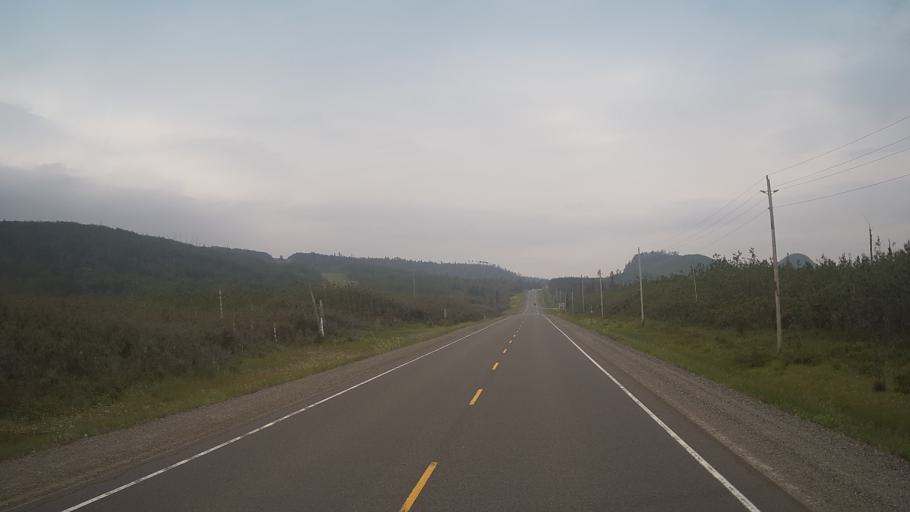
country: CA
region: Ontario
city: Greenstone
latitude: 49.4822
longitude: -88.0885
